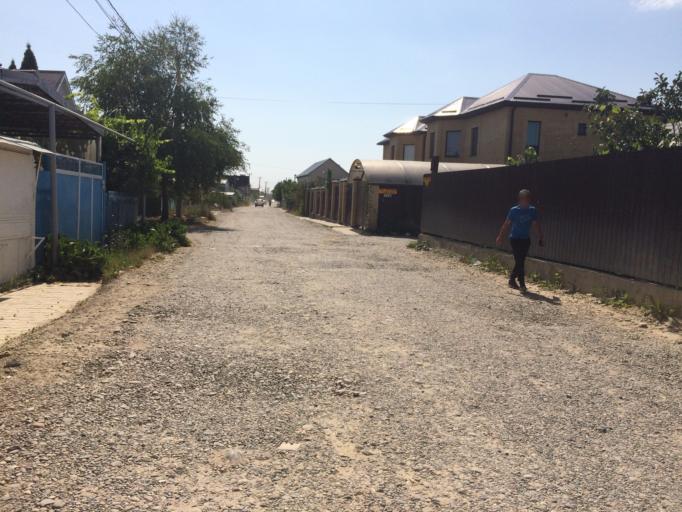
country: RU
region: Stavropol'skiy
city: Tatarka
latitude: 44.9882
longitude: 41.9381
